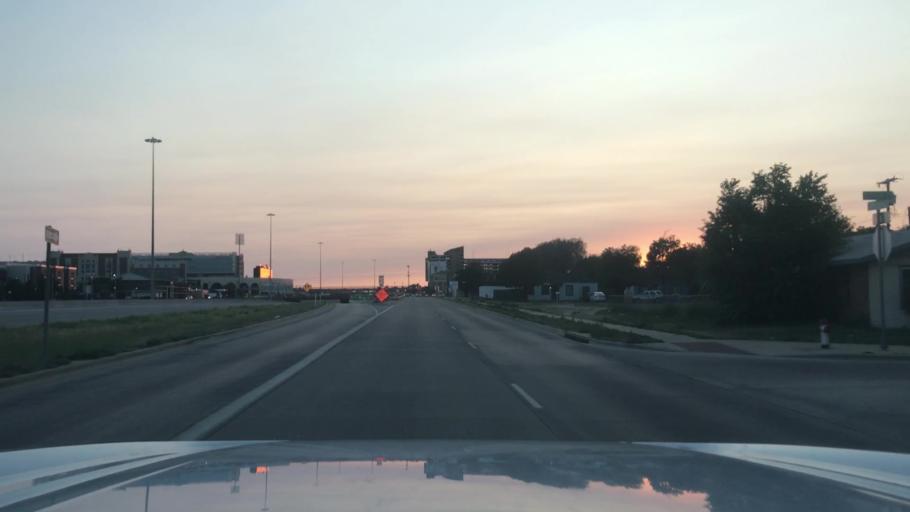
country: US
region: Texas
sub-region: Lubbock County
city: Lubbock
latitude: 33.5931
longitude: -101.8651
